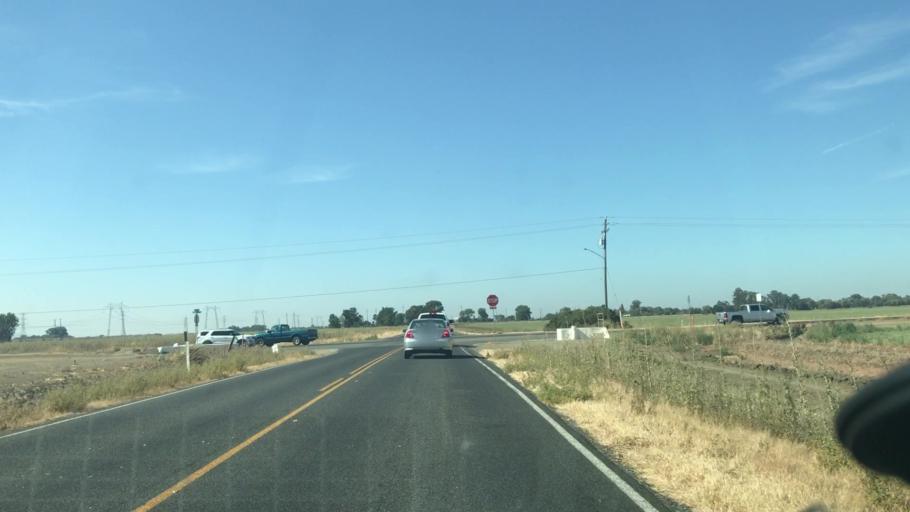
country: US
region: California
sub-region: Solano County
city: Vacaville
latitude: 38.3367
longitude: -121.9154
